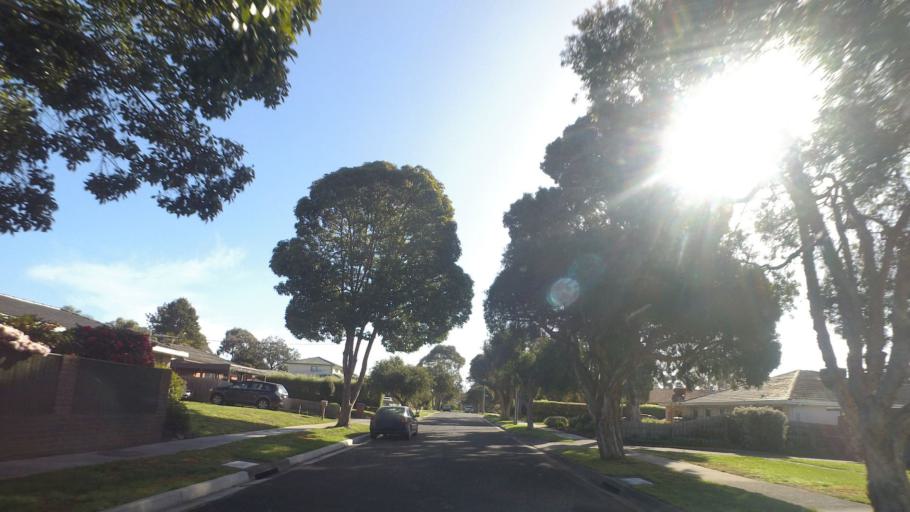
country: AU
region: Victoria
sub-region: Maroondah
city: Heathmont
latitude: -37.8400
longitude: 145.2529
